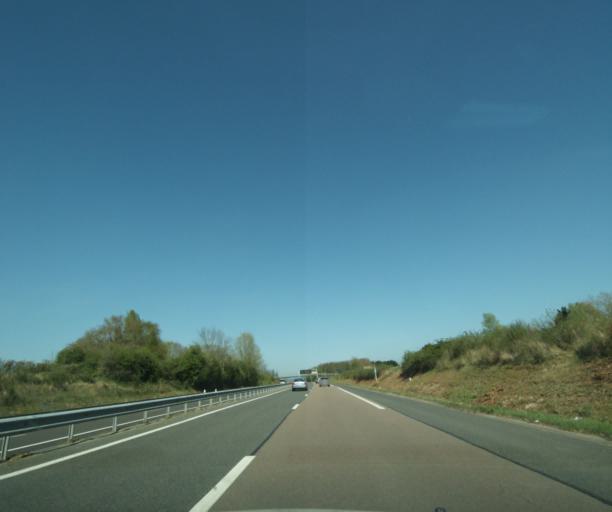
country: FR
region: Bourgogne
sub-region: Departement de la Nievre
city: Cosne-Cours-sur-Loire
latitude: 47.3940
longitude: 2.9323
